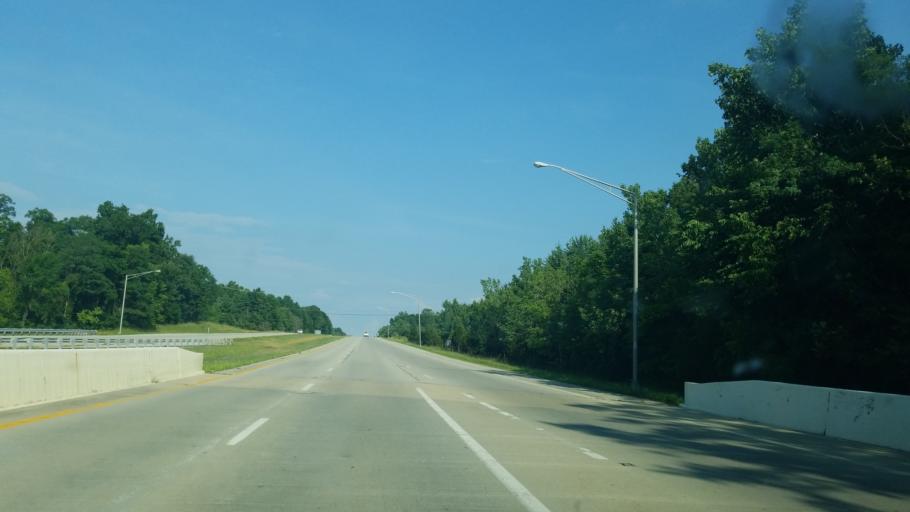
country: US
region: Ohio
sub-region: Brown County
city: Mount Orab
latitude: 39.0408
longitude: -83.9180
